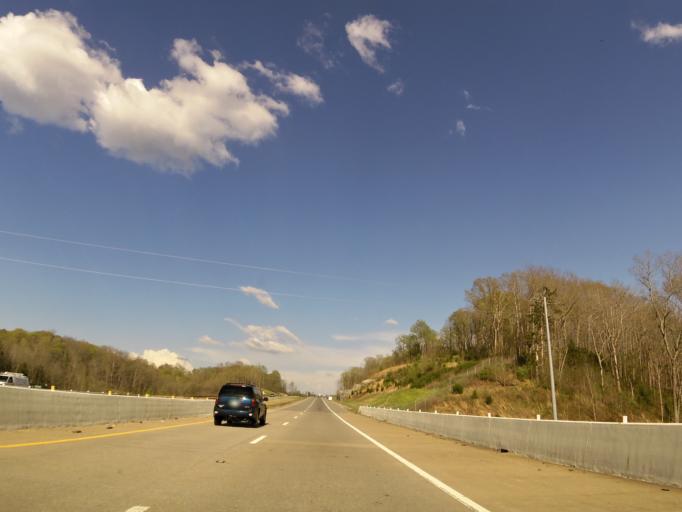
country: US
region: Tennessee
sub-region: Williamson County
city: Thompson's Station
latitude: 35.8171
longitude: -87.0202
